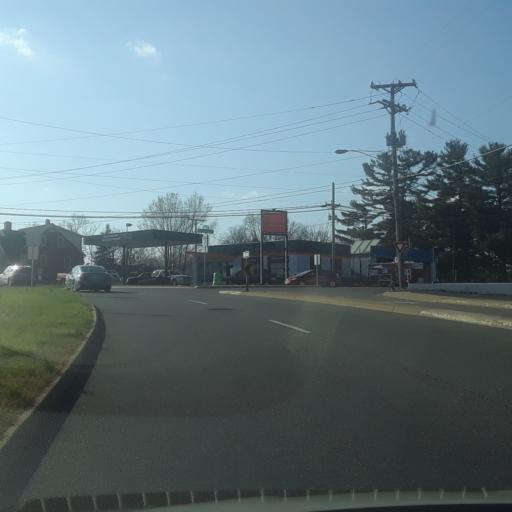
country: US
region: Virginia
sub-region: City of Harrisonburg
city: Harrisonburg
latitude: 38.4491
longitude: -78.8552
